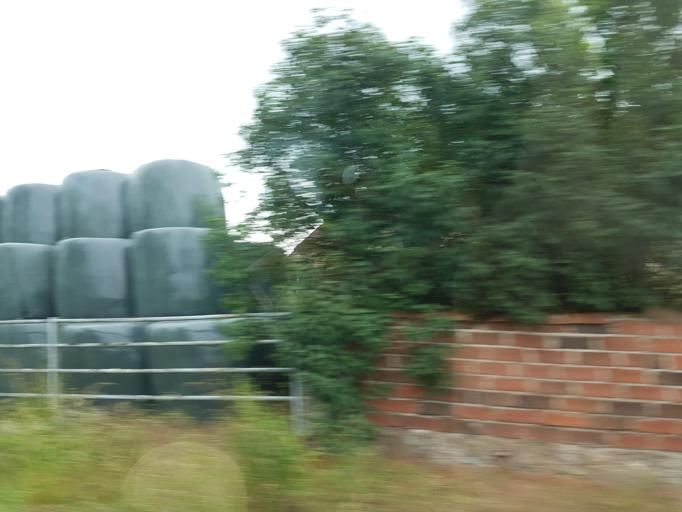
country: FR
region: Bourgogne
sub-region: Departement de la Nievre
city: Corbigny
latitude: 47.2042
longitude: 3.7191
